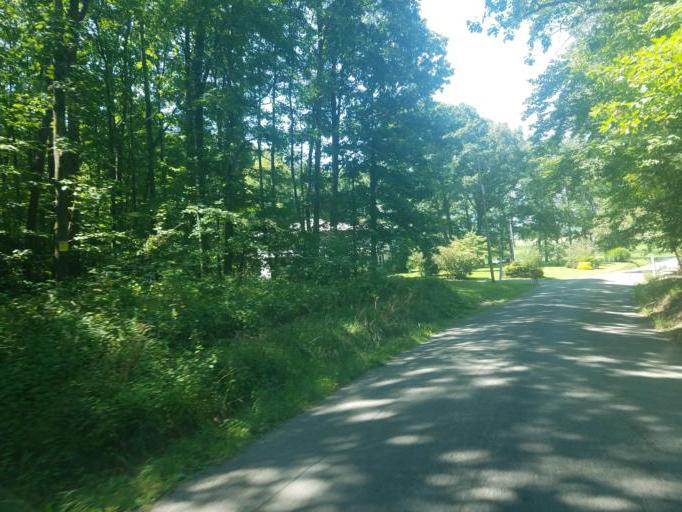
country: US
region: Pennsylvania
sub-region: Clarion County
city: Knox
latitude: 41.1785
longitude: -79.4933
